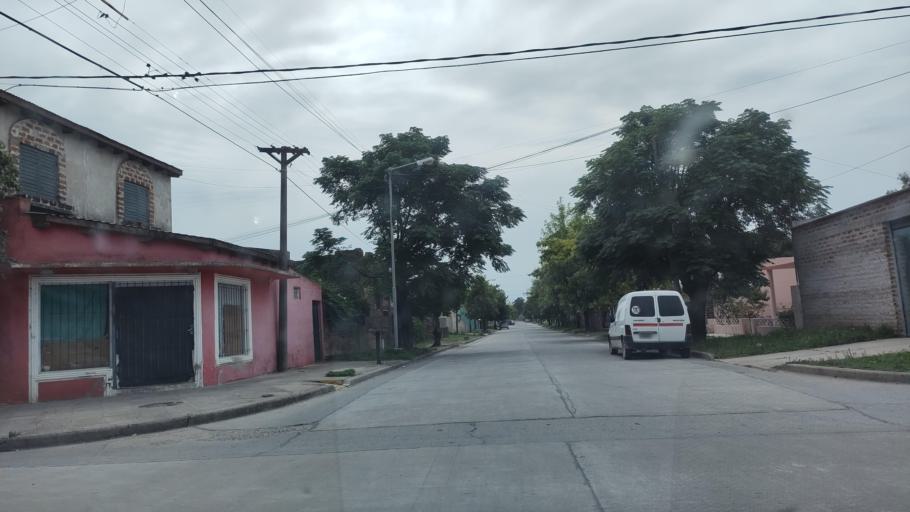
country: AR
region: Buenos Aires
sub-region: Partido de Loberia
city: Loberia
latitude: -38.1629
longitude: -58.7749
